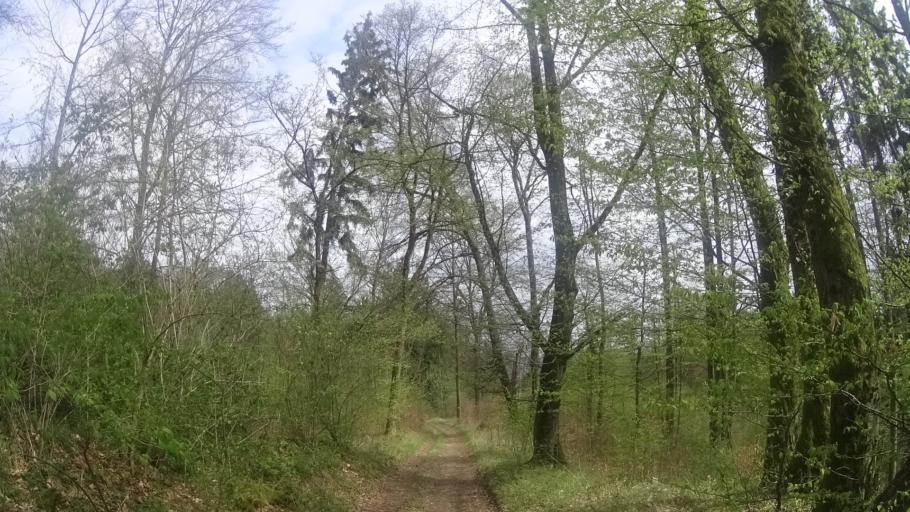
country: DE
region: Bavaria
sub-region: Upper Franconia
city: Igensdorf
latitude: 49.6265
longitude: 11.1963
